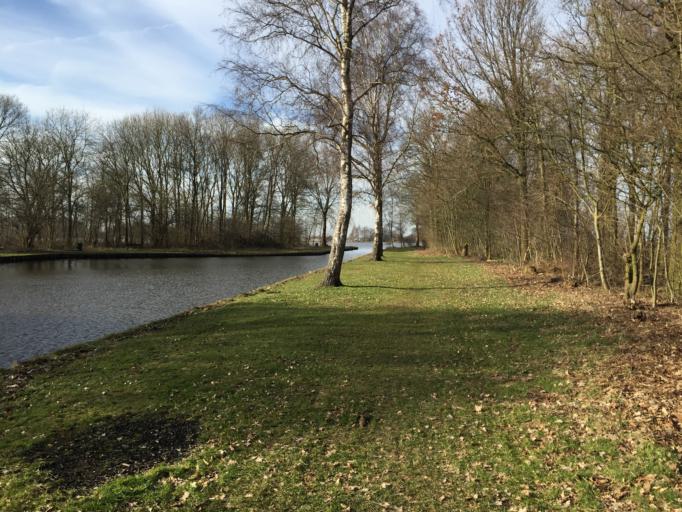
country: NL
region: South Holland
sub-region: Gemeente Vlist
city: Haastrecht
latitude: 52.0239
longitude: 4.7700
